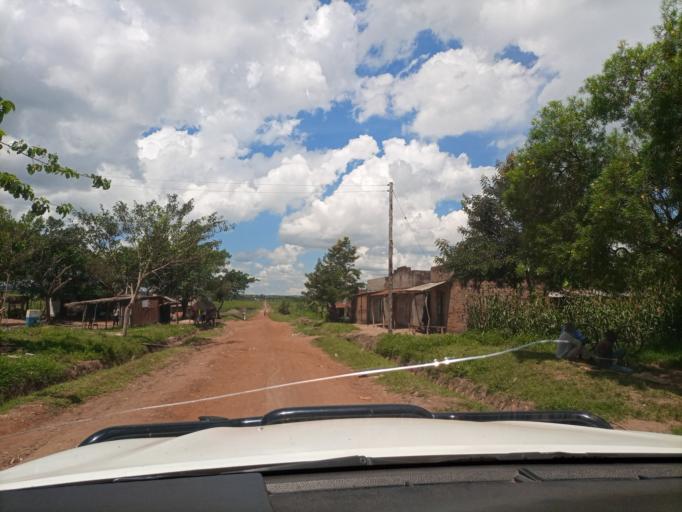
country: UG
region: Eastern Region
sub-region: Tororo District
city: Tororo
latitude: 0.6427
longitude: 33.9947
